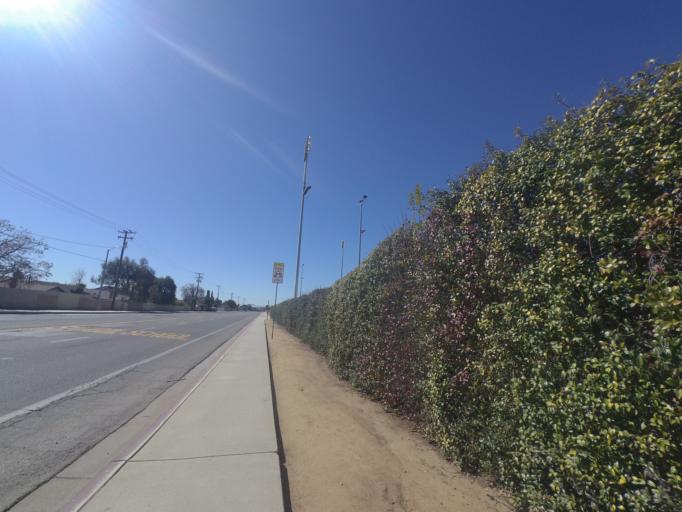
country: US
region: California
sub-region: Riverside County
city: Moreno Valley
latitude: 33.9277
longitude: -117.2526
